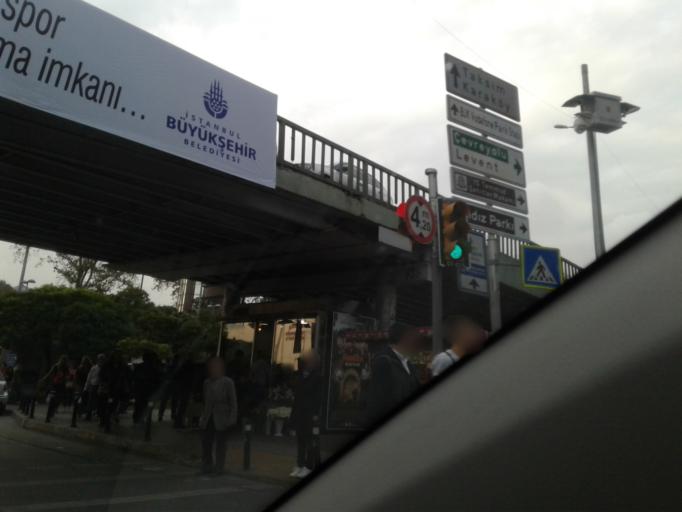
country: TR
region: Istanbul
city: UEskuedar
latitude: 41.0425
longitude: 29.0082
